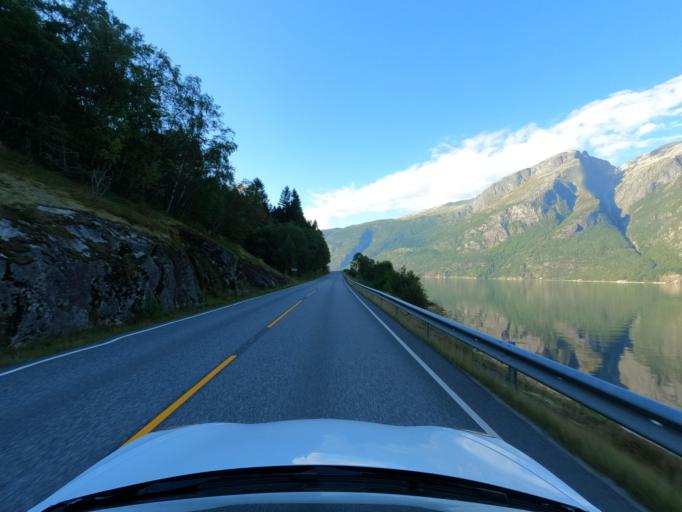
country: NO
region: Hordaland
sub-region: Eidfjord
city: Eidfjord
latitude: 60.4709
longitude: 7.0459
